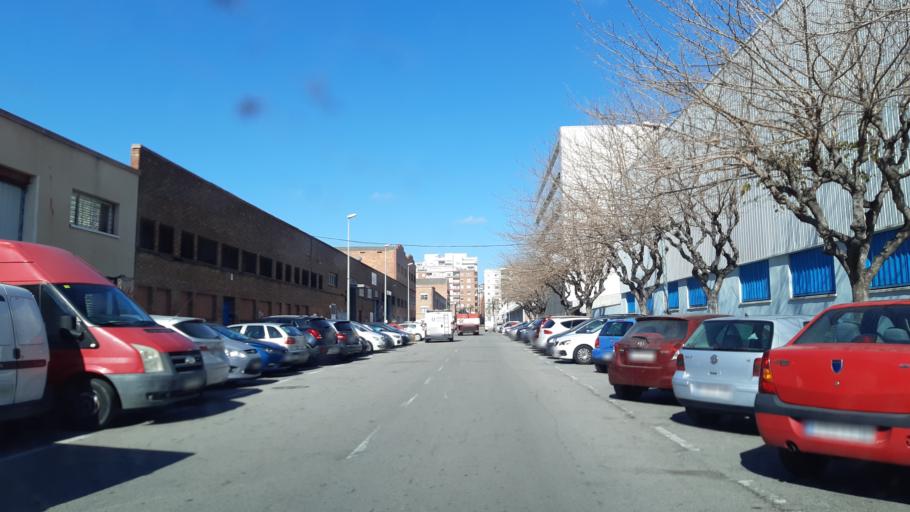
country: ES
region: Catalonia
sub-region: Provincia de Barcelona
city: L'Hospitalet de Llobregat
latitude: 41.3579
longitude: 2.1113
